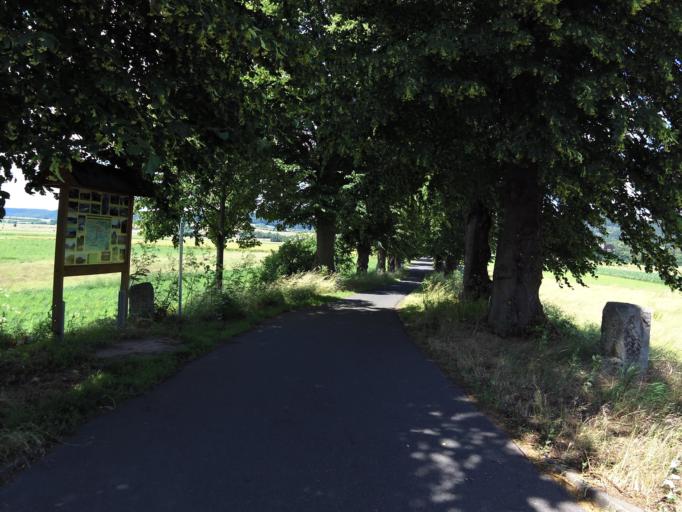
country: DE
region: Thuringia
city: Lauchroden
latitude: 50.9968
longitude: 10.1599
